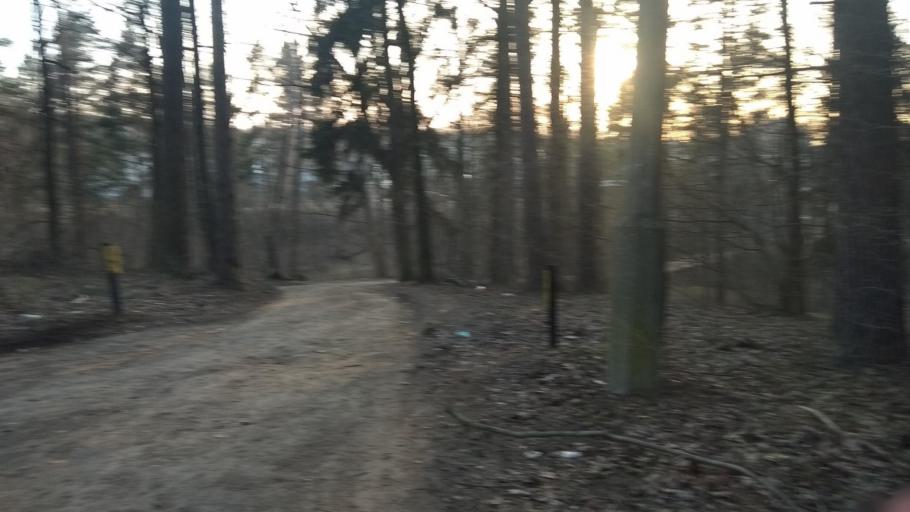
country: RU
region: Moskovskaya
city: Vidnoye
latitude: 55.5590
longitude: 37.7360
